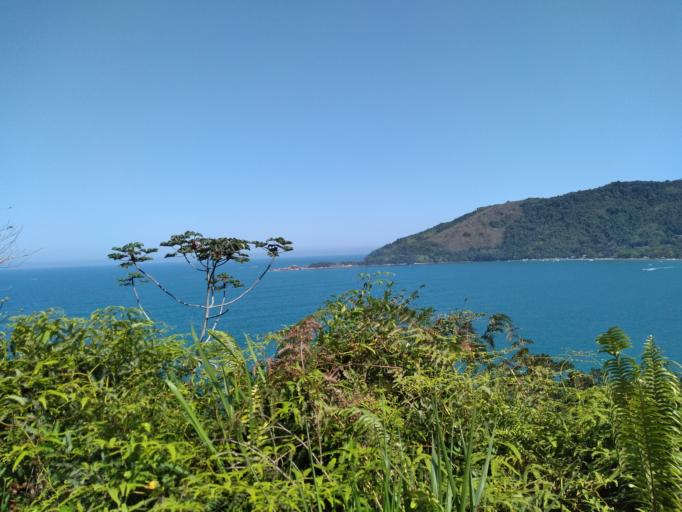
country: BR
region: Sao Paulo
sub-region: Ubatuba
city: Ubatuba
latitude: -23.5190
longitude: -45.1645
